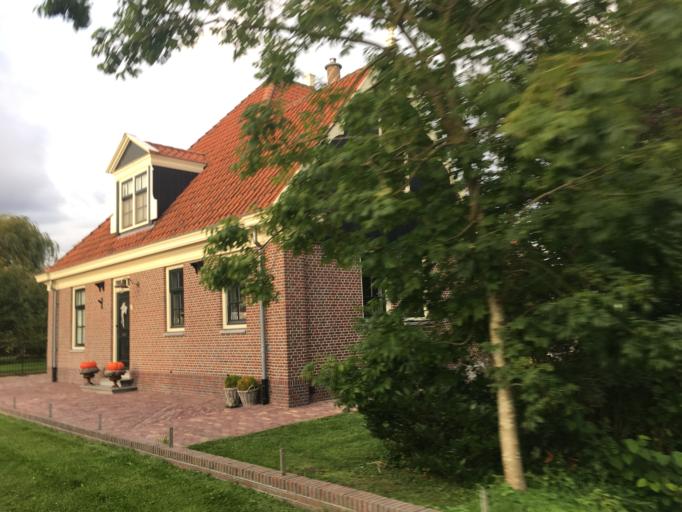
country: NL
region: North Holland
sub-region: Gemeente Zaanstad
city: Zaanstad
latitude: 52.4461
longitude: 4.7769
